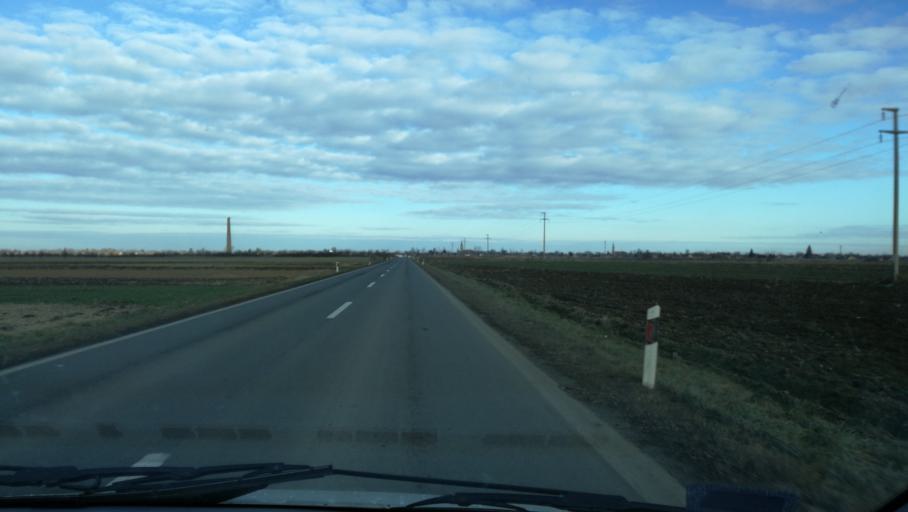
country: RS
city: Ostojicevo
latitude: 45.8750
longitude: 20.1650
